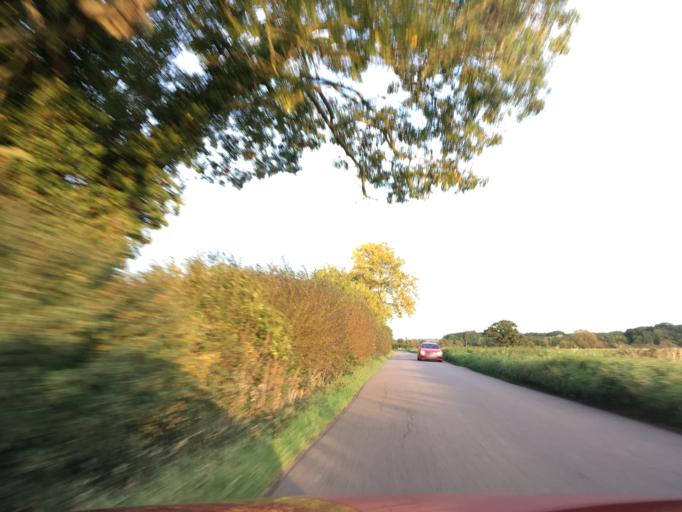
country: GB
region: England
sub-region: South Gloucestershire
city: Thornbury
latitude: 51.6276
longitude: -2.5509
